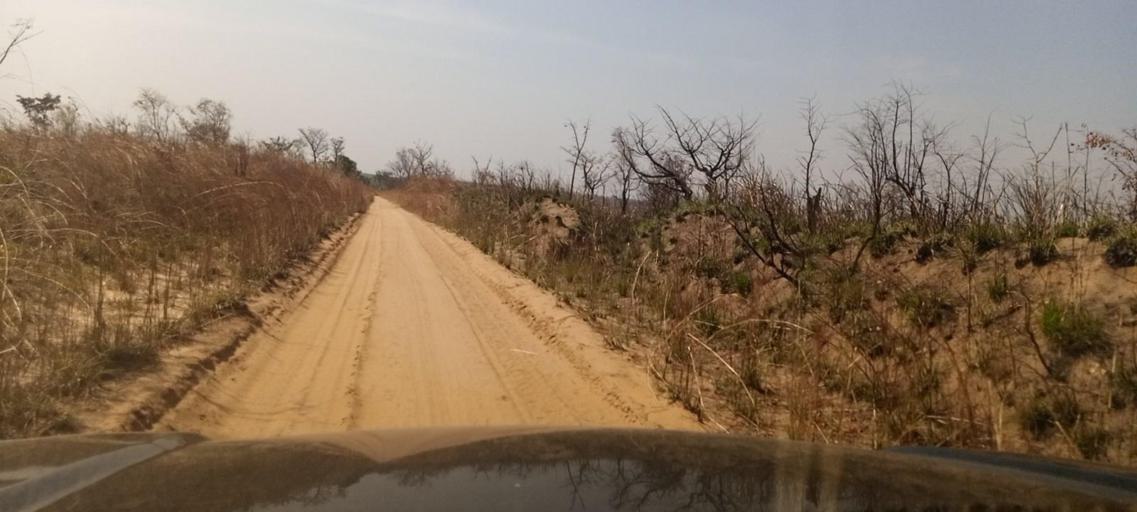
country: CD
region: Kasai-Oriental
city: Kabinda
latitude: -5.7860
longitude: 25.0490
